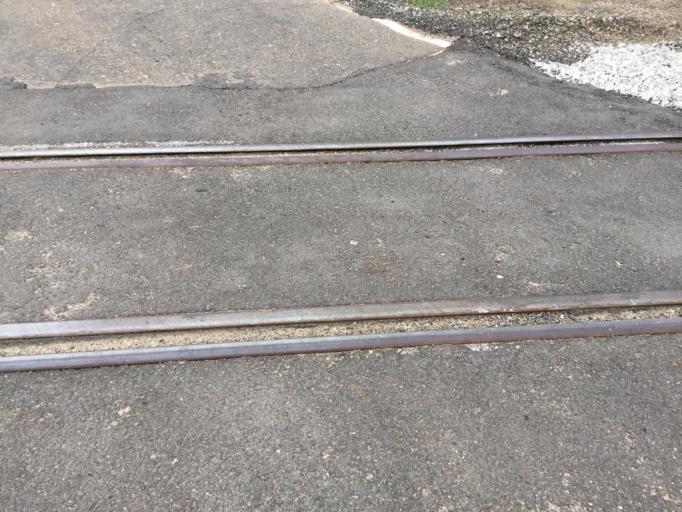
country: US
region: Kansas
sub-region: Sedgwick County
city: Cheney
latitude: 37.4516
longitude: -97.8440
